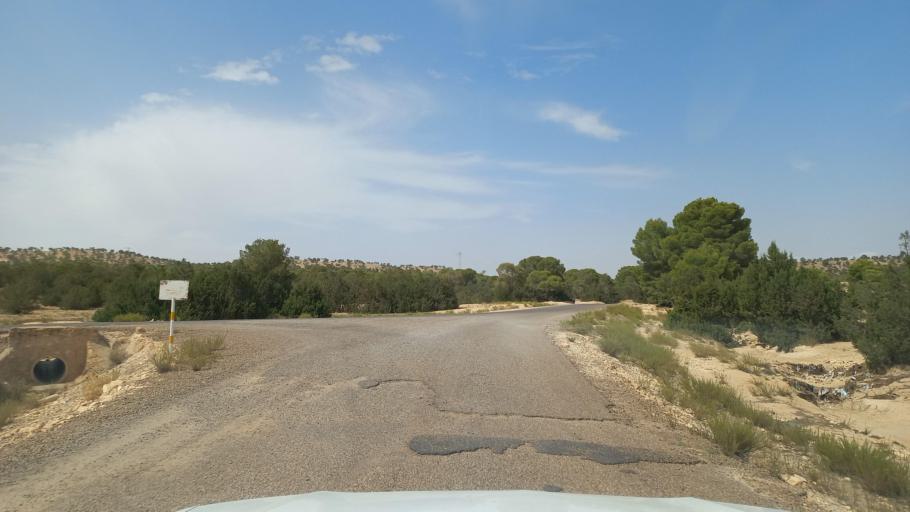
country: TN
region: Al Qasrayn
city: Sbiba
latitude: 35.4120
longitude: 8.9271
